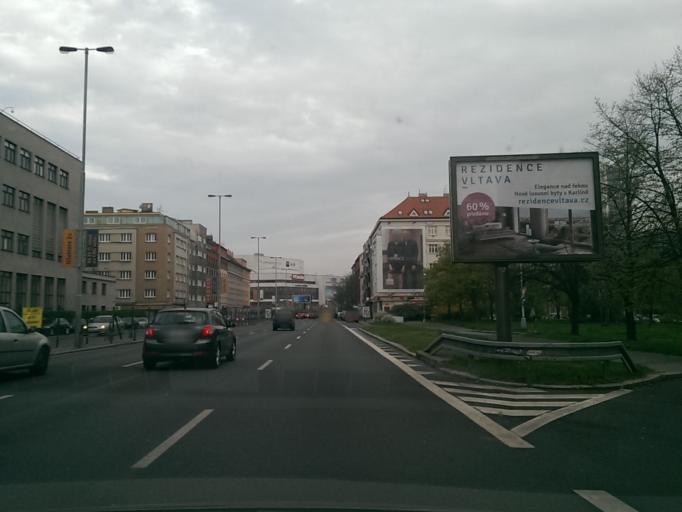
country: CZ
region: Praha
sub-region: Praha 2
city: Vysehrad
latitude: 50.0594
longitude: 14.4337
